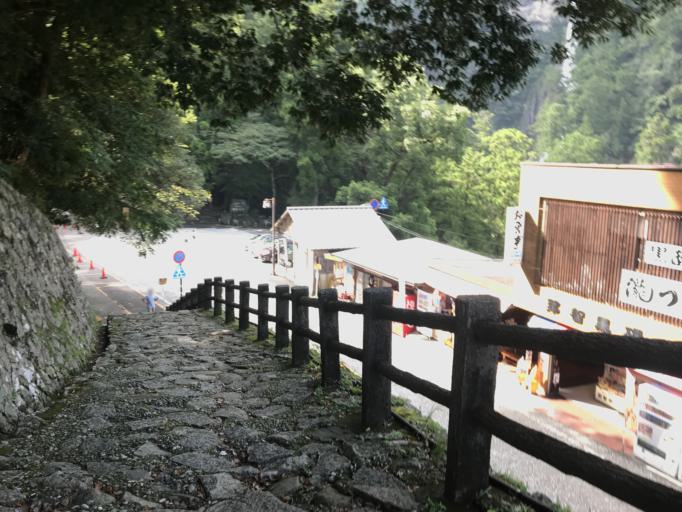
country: JP
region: Wakayama
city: Shingu
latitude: 33.6726
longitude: 135.8898
